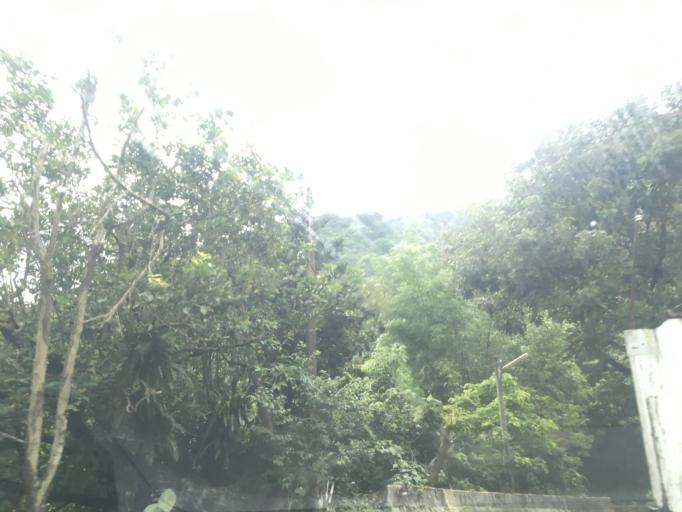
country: TW
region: Taiwan
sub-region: Yunlin
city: Douliu
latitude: 23.5678
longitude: 120.6426
